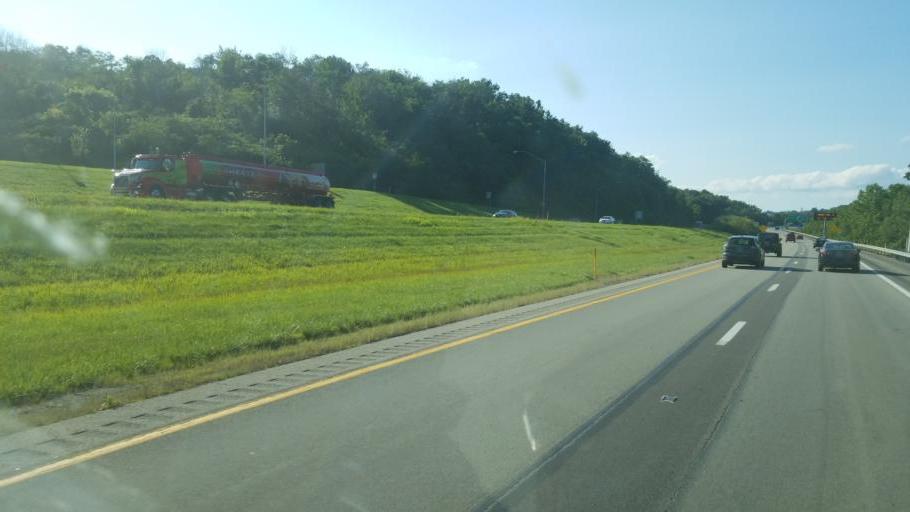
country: US
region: Pennsylvania
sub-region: Washington County
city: East Washington
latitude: 40.1221
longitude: -80.2058
